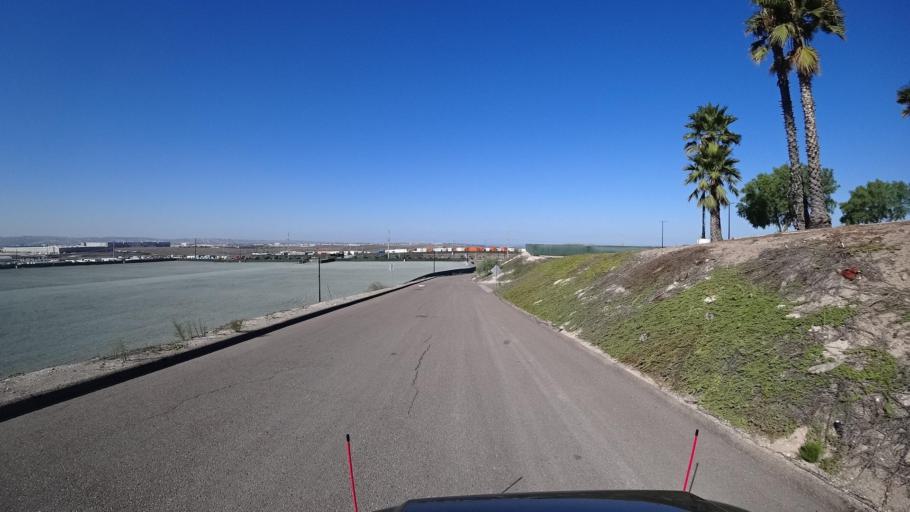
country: MX
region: Baja California
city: Tijuana
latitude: 32.5802
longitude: -116.9165
